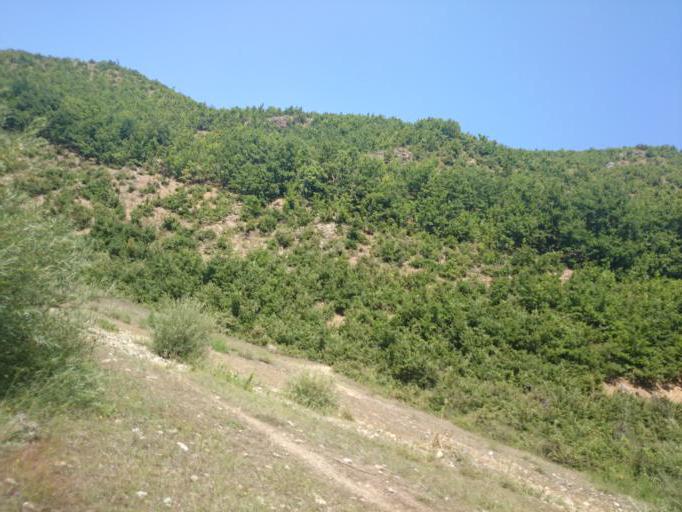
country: AL
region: Diber
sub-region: Rrethi i Dibres
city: Melan
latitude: 41.6185
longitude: 20.4115
